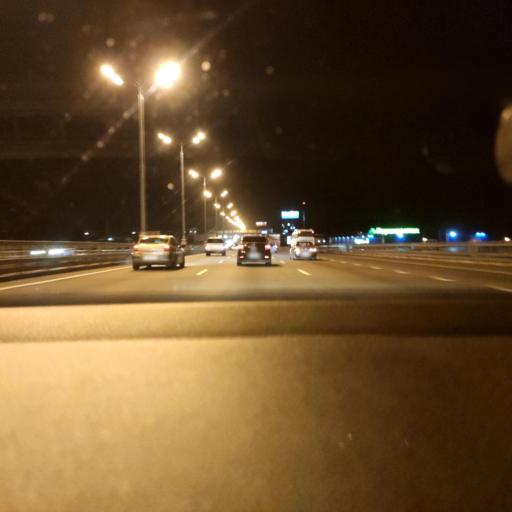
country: RU
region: Moskovskaya
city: Selyatino
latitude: 55.5251
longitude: 37.0227
